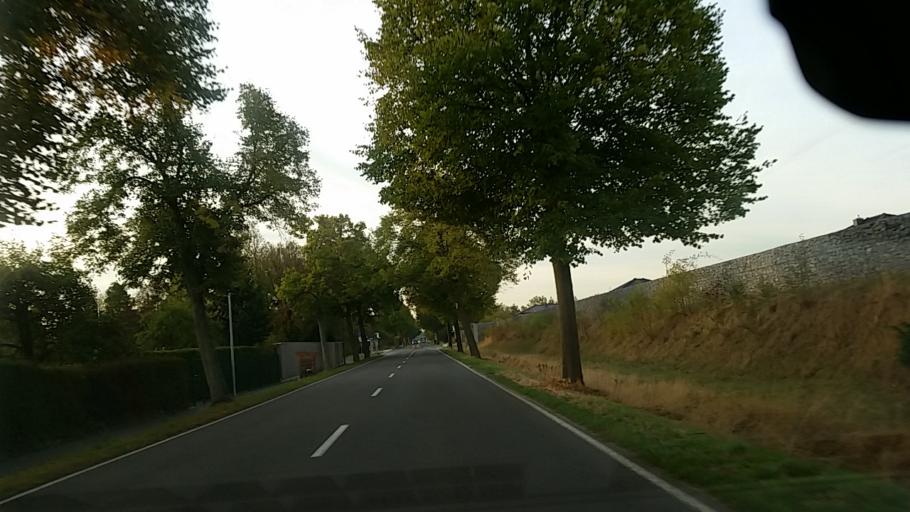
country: DE
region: Lower Saxony
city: Tiddische
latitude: 52.4753
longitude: 10.8208
